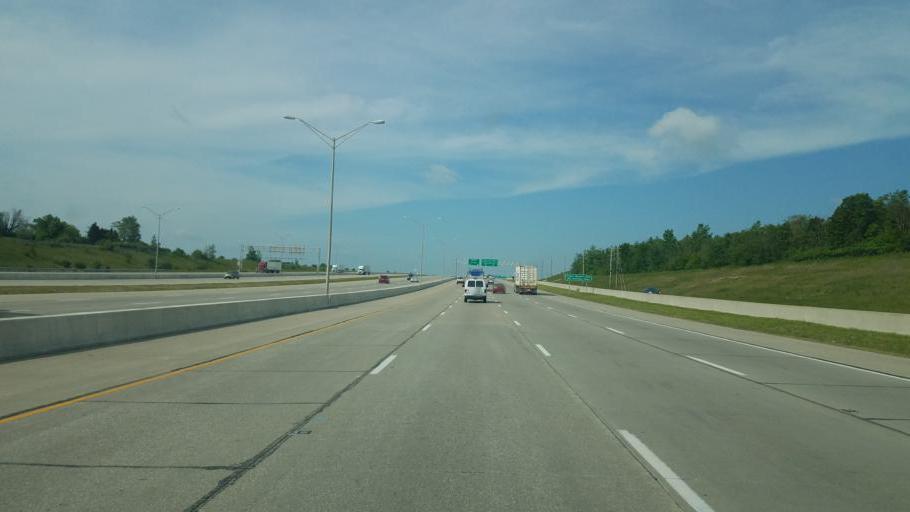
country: US
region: Indiana
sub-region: Marion County
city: Speedway
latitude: 39.7024
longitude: -86.2916
